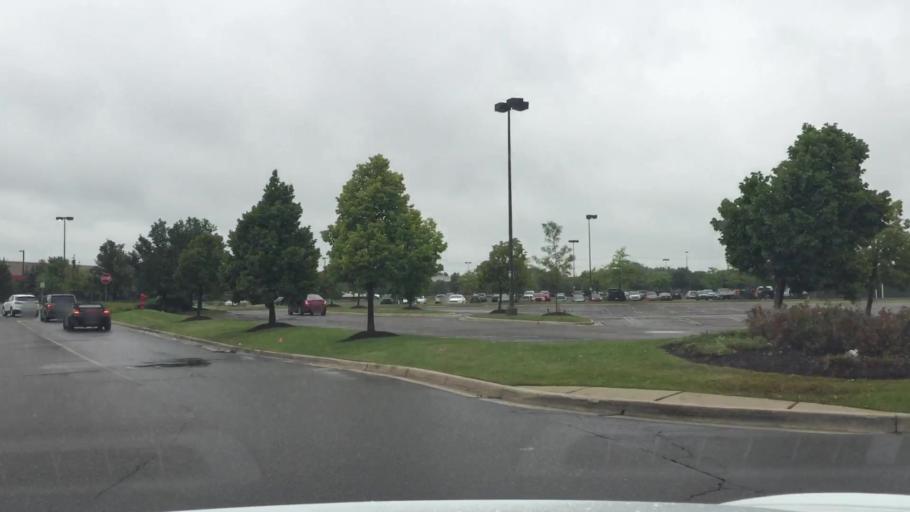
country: US
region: Michigan
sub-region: Wayne County
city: Livonia
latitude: 42.3801
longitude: -83.3295
